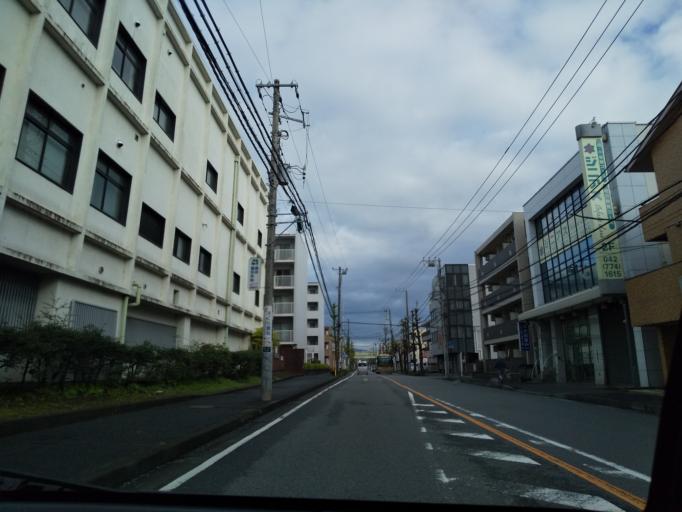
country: JP
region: Tokyo
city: Hachioji
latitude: 35.5980
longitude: 139.3460
